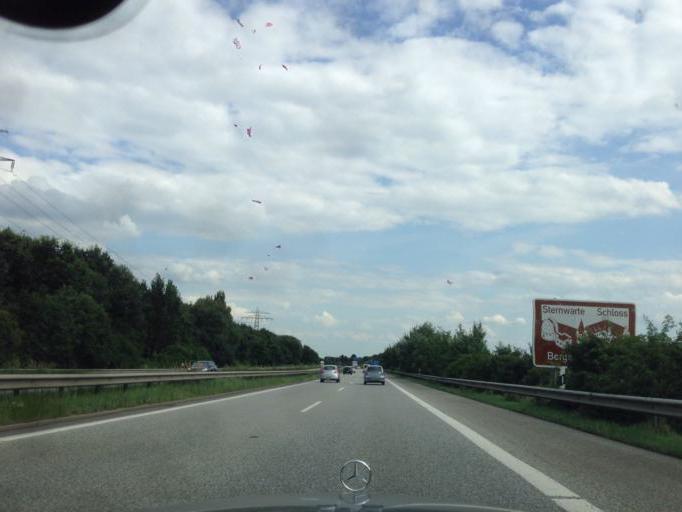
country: DE
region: Hamburg
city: Rothenburgsort
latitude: 53.4946
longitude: 10.0987
